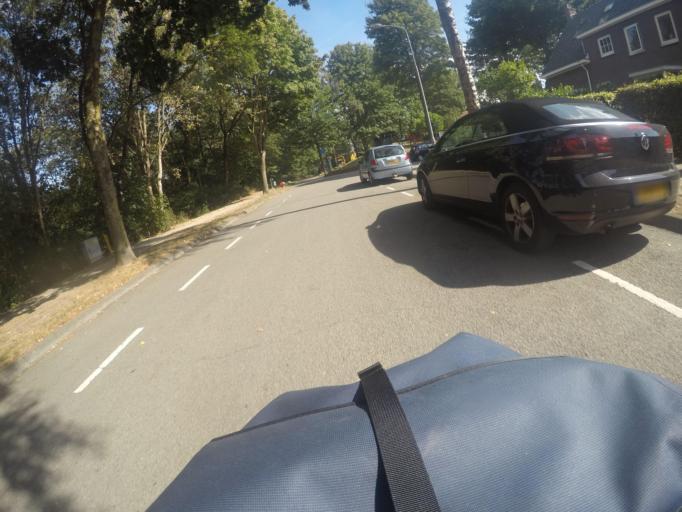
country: NL
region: Gelderland
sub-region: Gemeente Renkum
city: Oosterbeek
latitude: 51.9909
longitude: 5.8491
